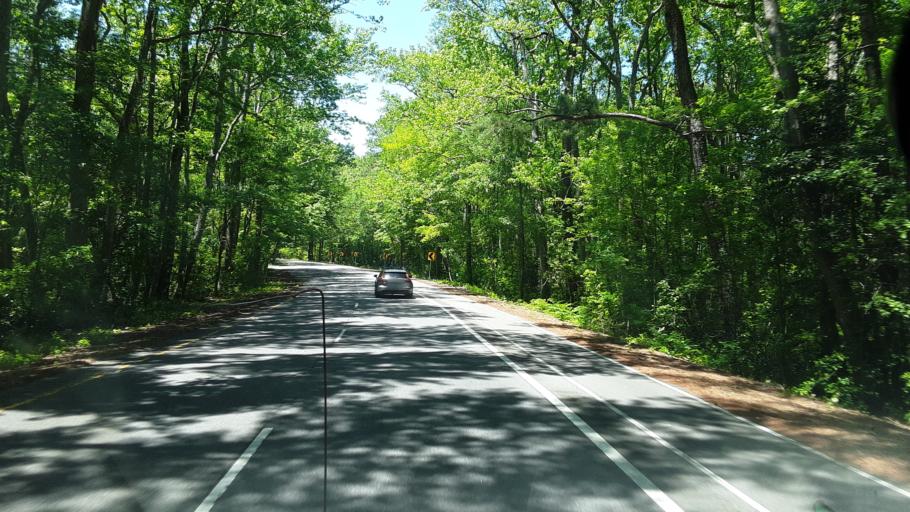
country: US
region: Virginia
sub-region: City of Virginia Beach
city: Virginia Beach
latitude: 36.9191
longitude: -76.0196
